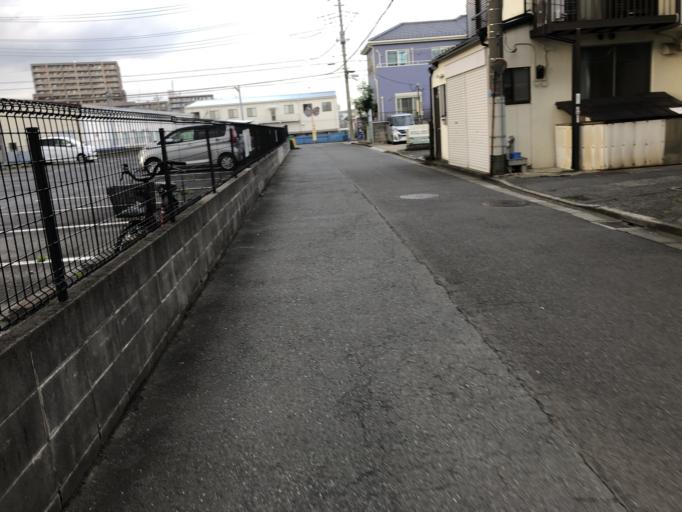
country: JP
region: Saitama
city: Asaka
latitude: 35.8020
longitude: 139.5781
